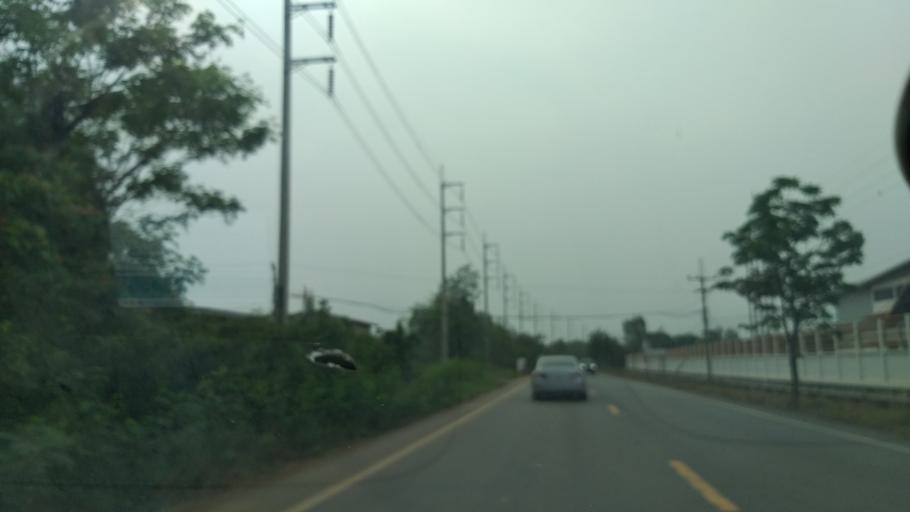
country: TH
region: Chachoengsao
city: Plaeng Yao
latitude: 13.5779
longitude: 101.2395
